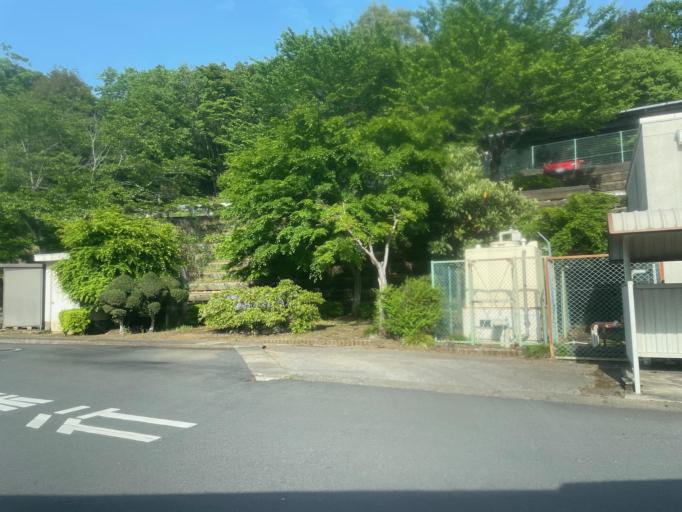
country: JP
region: Tochigi
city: Ashikaga
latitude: 36.3364
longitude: 139.5049
